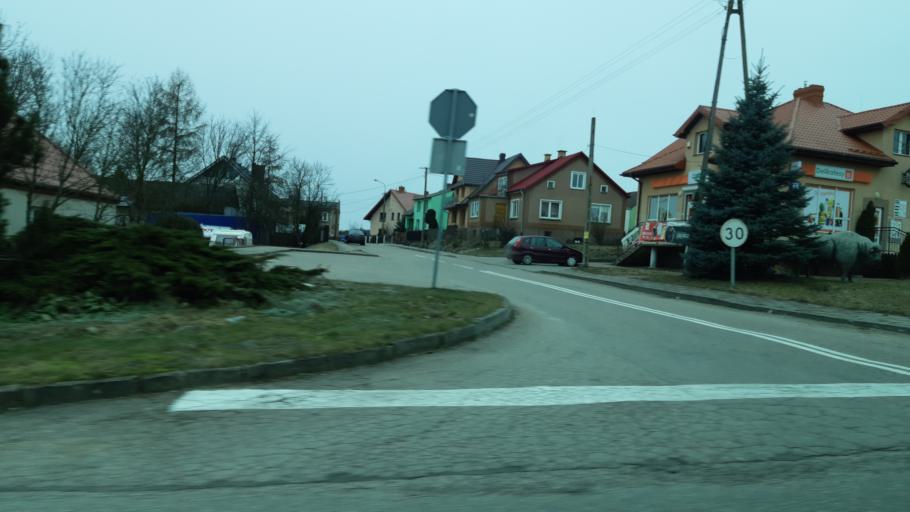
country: PL
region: Podlasie
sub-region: Suwalki
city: Suwalki
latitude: 54.3268
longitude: 22.9661
